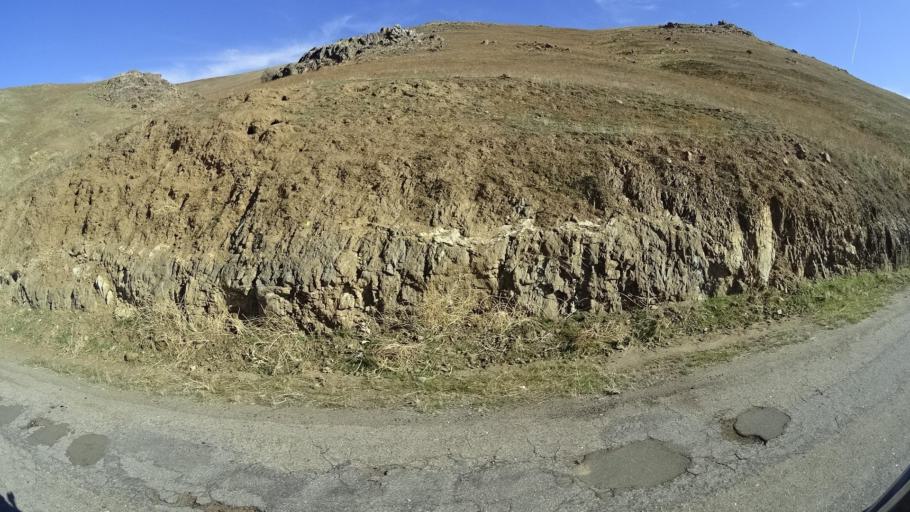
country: US
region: California
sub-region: Kern County
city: Arvin
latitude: 35.4128
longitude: -118.7519
